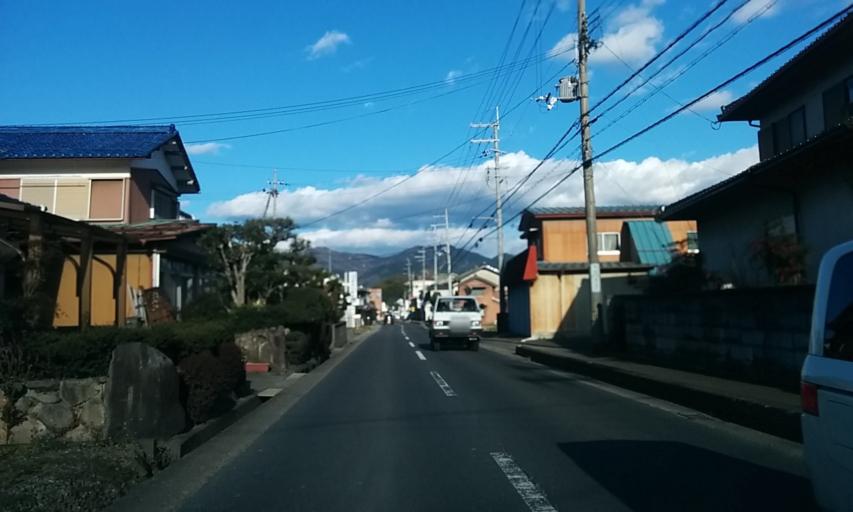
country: JP
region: Kyoto
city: Fukuchiyama
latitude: 35.3012
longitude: 135.0967
